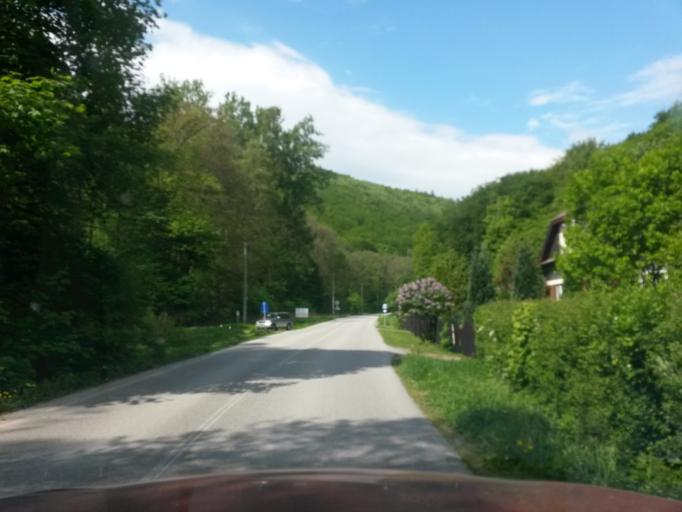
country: SK
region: Kosicky
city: Moldava nad Bodvou
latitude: 48.7255
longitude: 21.0722
